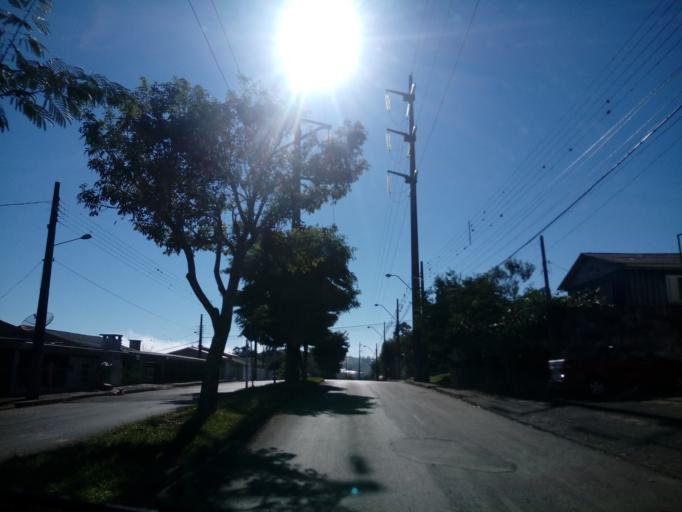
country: BR
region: Santa Catarina
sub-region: Chapeco
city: Chapeco
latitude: -27.0660
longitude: -52.6041
